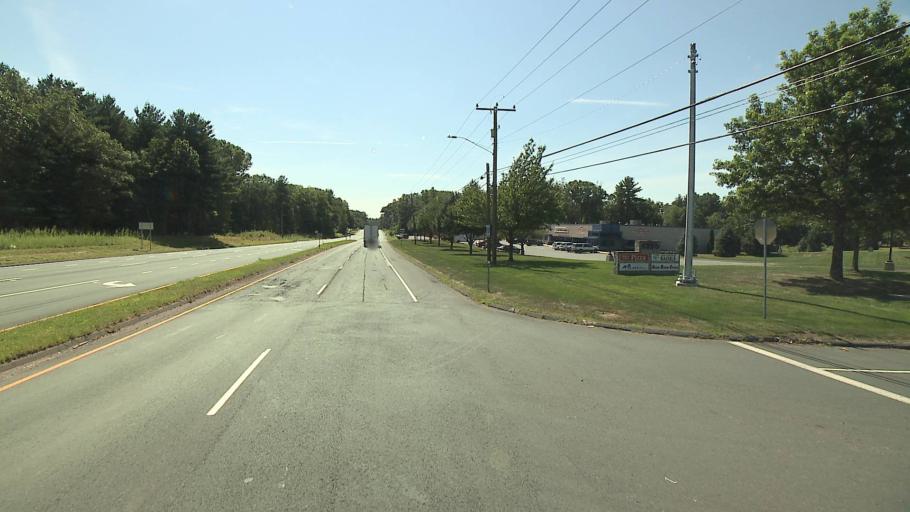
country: US
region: Connecticut
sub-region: Hartford County
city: Blue Hills
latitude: 41.8641
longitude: -72.7162
